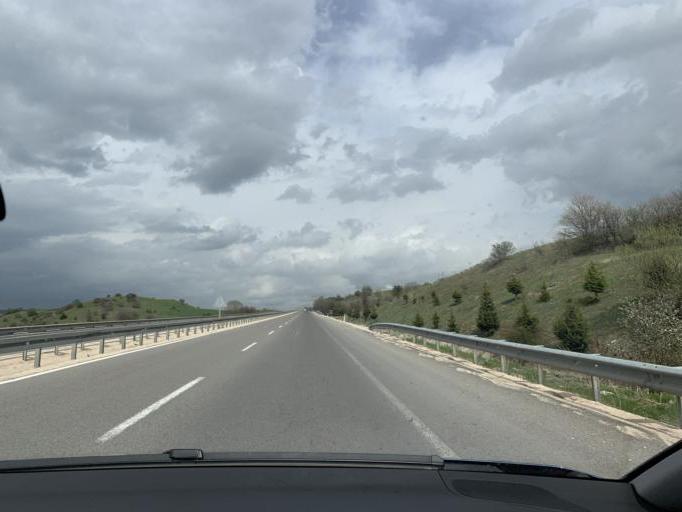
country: TR
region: Bolu
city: Yenicaga
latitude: 40.7810
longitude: 32.0956
